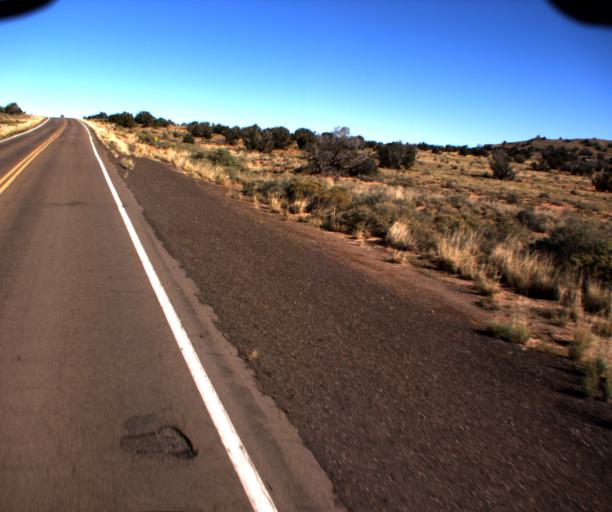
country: US
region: Arizona
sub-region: Navajo County
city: Snowflake
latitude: 34.6855
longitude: -110.1048
